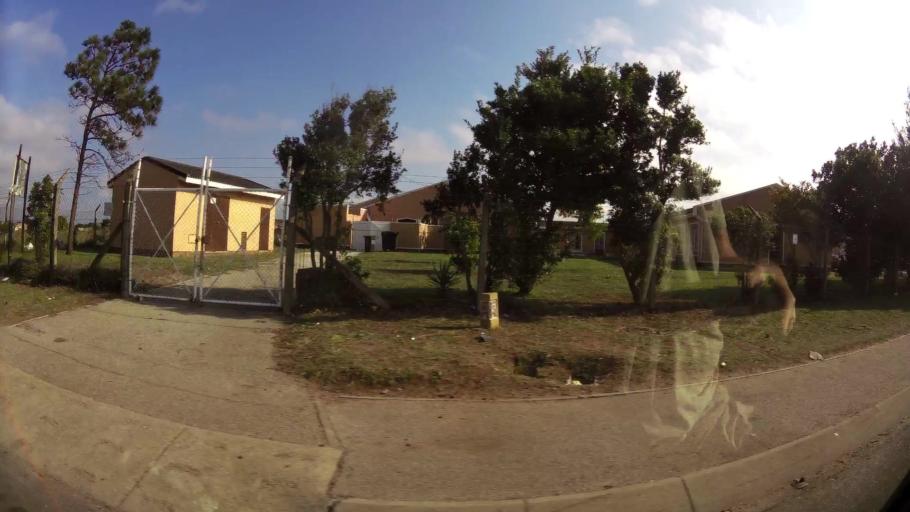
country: ZA
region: Eastern Cape
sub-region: Nelson Mandela Bay Metropolitan Municipality
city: Port Elizabeth
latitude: -33.9202
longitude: 25.5353
